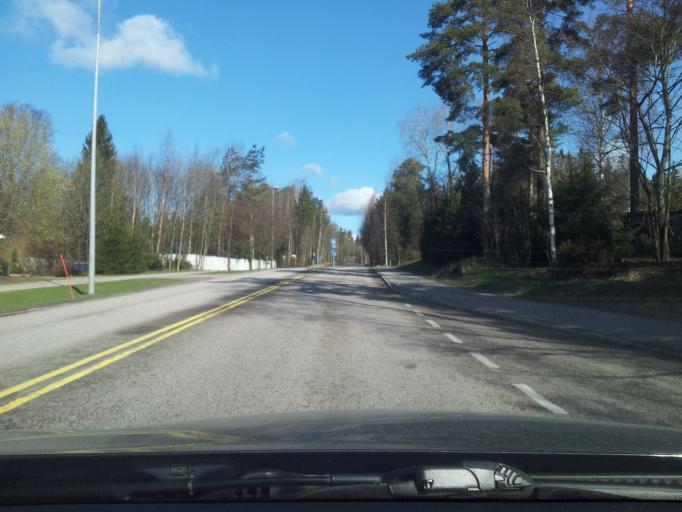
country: FI
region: Uusimaa
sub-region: Helsinki
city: Espoo
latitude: 60.1818
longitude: 24.6706
